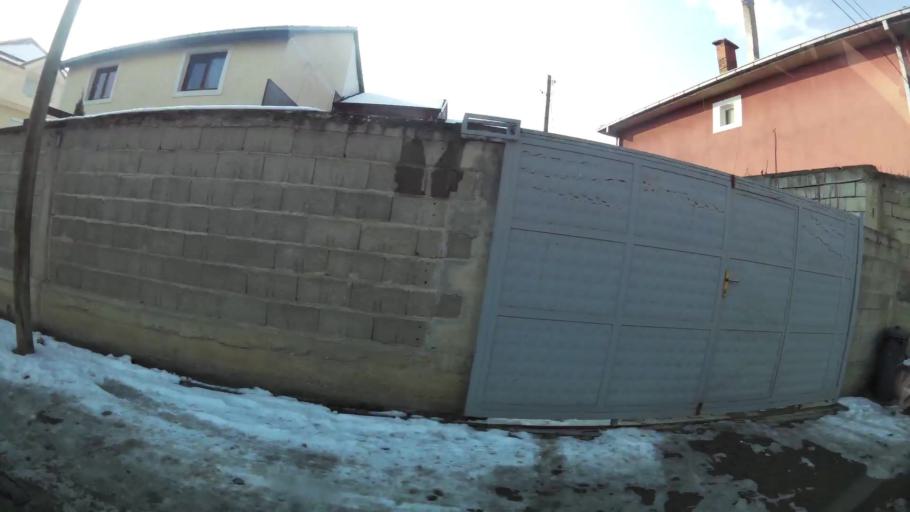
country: MK
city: Creshevo
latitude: 42.0167
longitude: 21.5095
